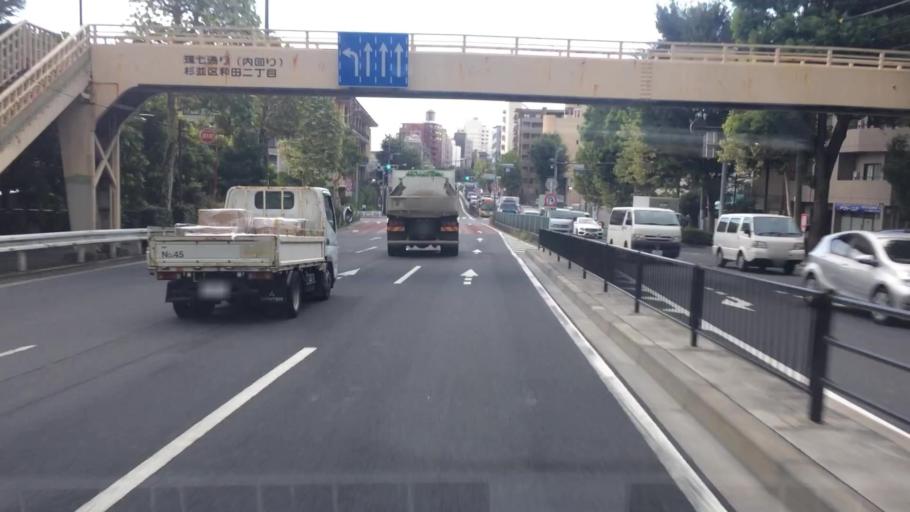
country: JP
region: Tokyo
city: Tokyo
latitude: 35.6883
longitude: 139.6554
